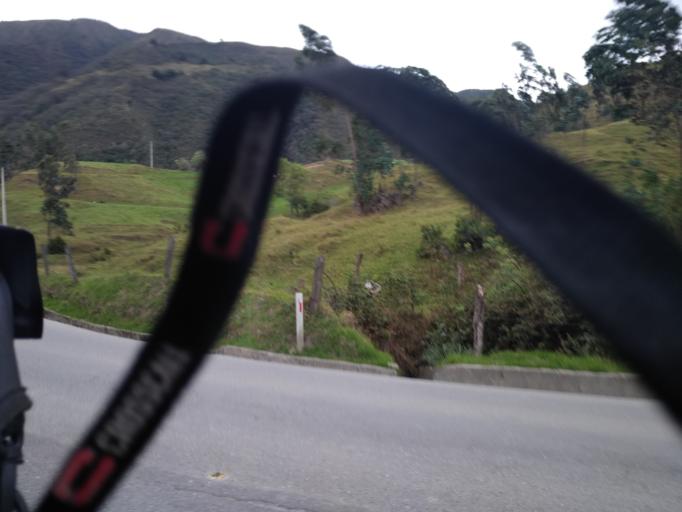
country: EC
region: Loja
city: Loja
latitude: -4.0849
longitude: -79.2056
